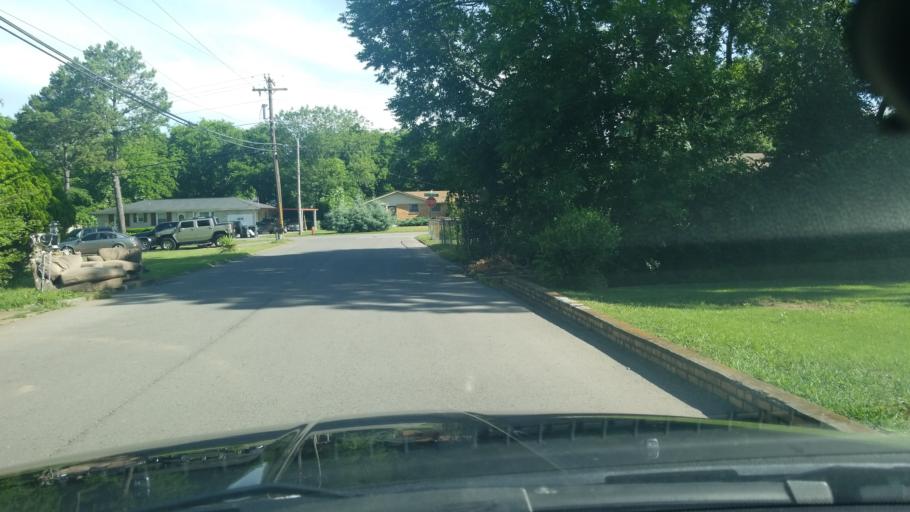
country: US
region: Tennessee
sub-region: Davidson County
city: Nashville
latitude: 36.2331
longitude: -86.7769
